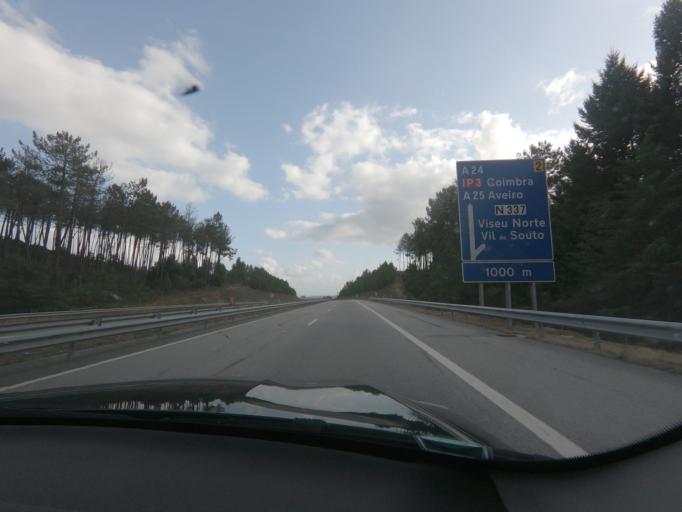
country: PT
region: Viseu
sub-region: Viseu
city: Abraveses
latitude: 40.6885
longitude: -7.9664
